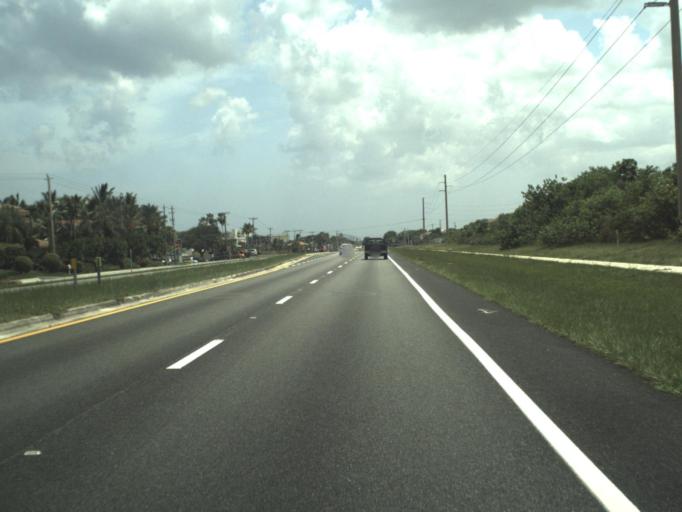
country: US
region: Florida
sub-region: Palm Beach County
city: Tequesta
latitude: 26.9757
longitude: -80.0892
